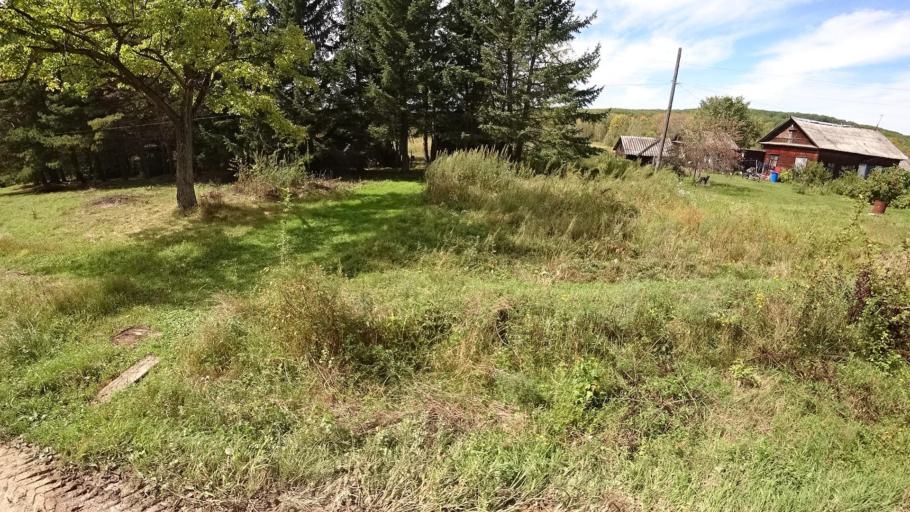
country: RU
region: Primorskiy
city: Yakovlevka
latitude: 44.6497
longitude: 133.5880
